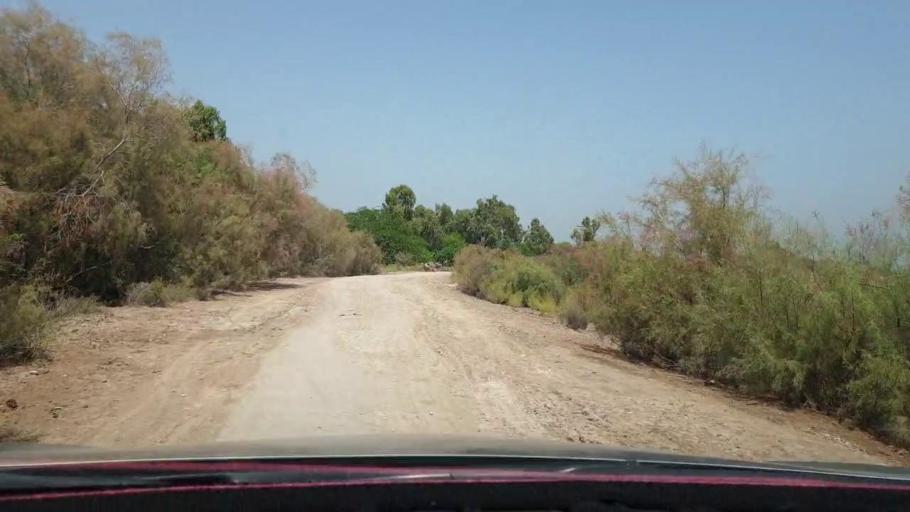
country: PK
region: Sindh
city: Warah
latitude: 27.4297
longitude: 67.6990
